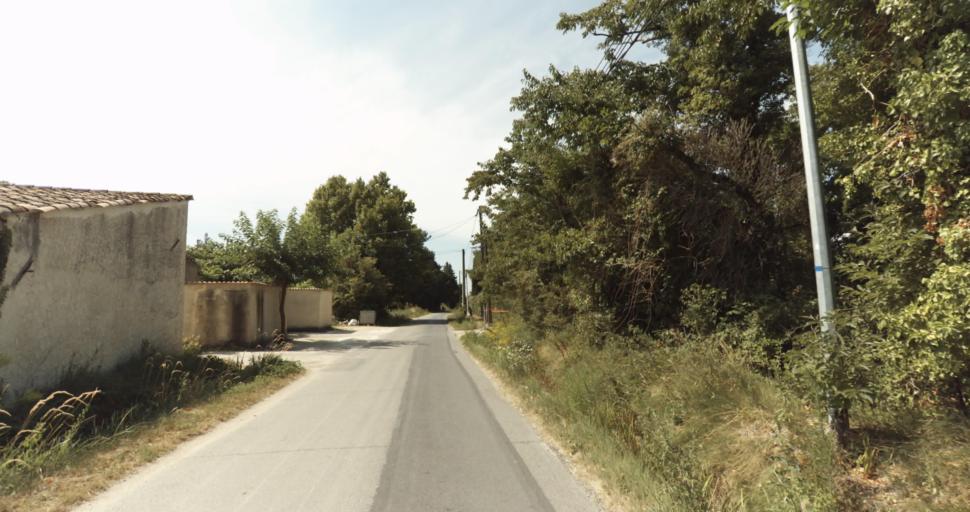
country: FR
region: Provence-Alpes-Cote d'Azur
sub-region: Departement du Vaucluse
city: Monteux
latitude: 44.0244
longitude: 4.9928
